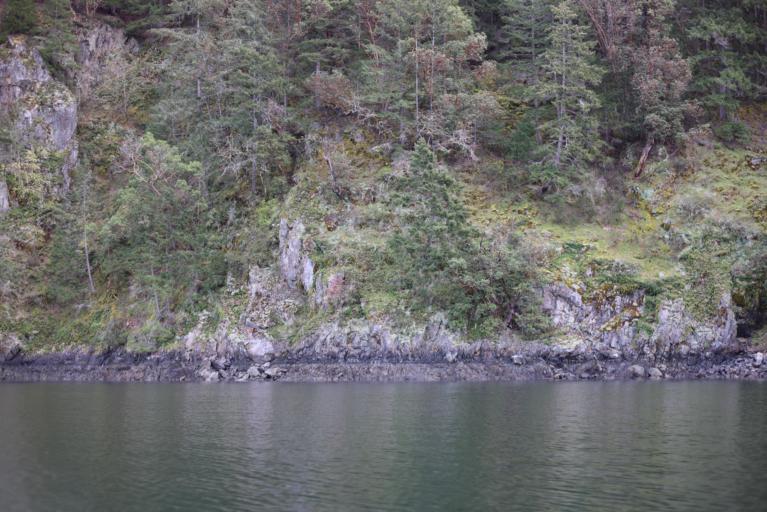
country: CA
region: British Columbia
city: Langford
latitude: 48.5172
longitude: -123.5362
